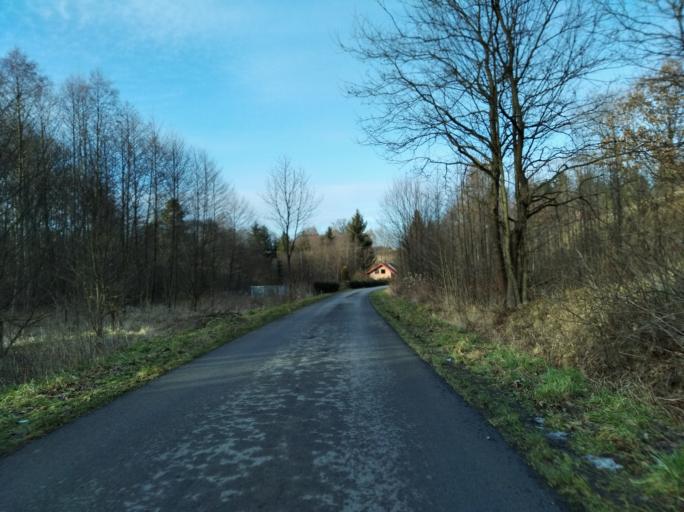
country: PL
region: Subcarpathian Voivodeship
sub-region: Powiat strzyzowski
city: Konieczkowa
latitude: 49.8289
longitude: 21.9390
